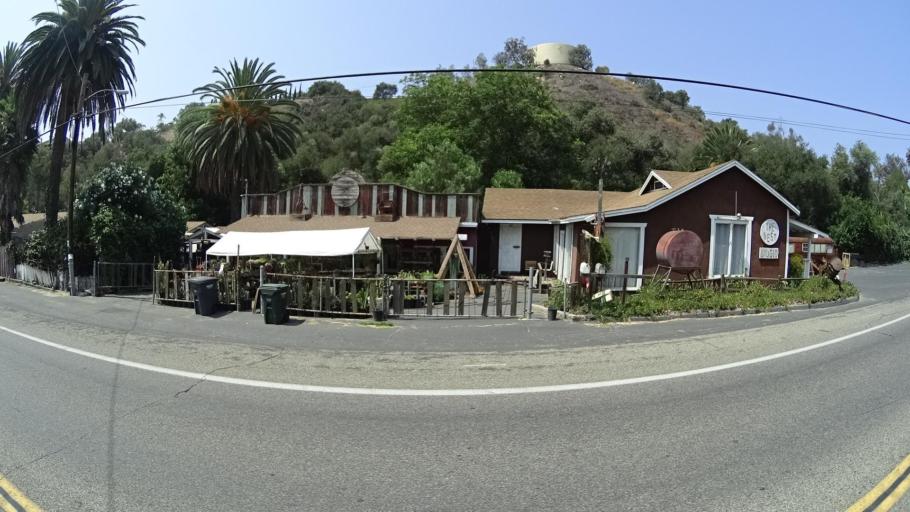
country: US
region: California
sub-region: San Diego County
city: Fallbrook
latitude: 33.3353
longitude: -117.2367
